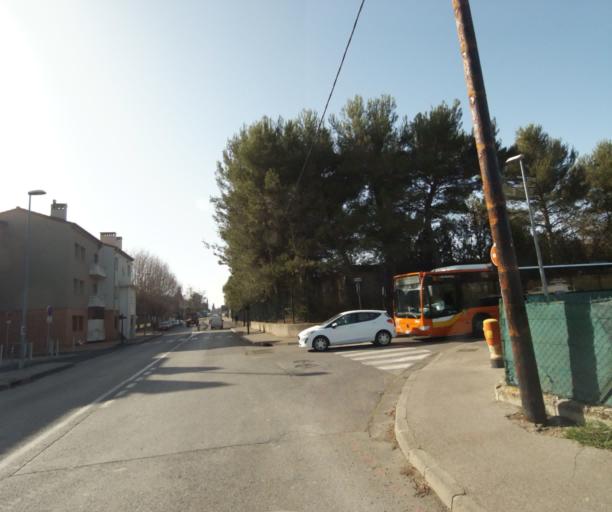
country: FR
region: Provence-Alpes-Cote d'Azur
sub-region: Departement des Bouches-du-Rhone
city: Aix-en-Provence
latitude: 43.5402
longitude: 5.4537
